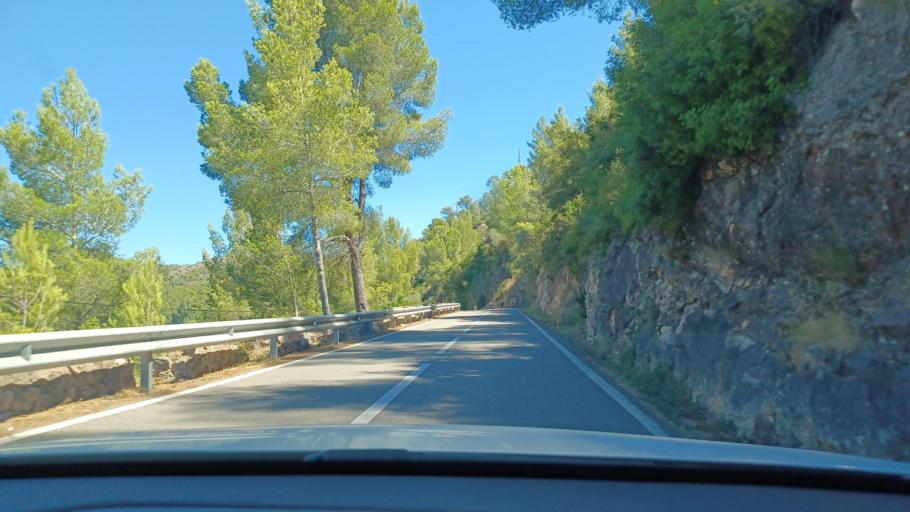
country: ES
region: Catalonia
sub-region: Provincia de Tarragona
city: Benifallet
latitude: 40.9575
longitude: 0.5092
